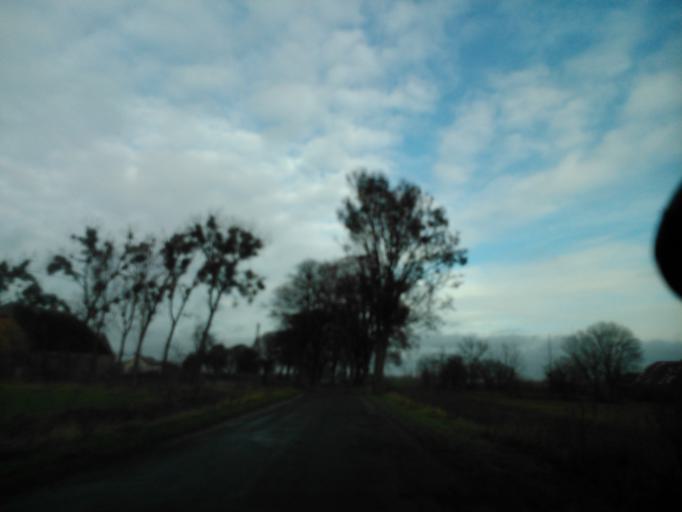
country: PL
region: Kujawsko-Pomorskie
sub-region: Powiat wabrzeski
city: Debowa Laka
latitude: 53.2110
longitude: 19.1191
